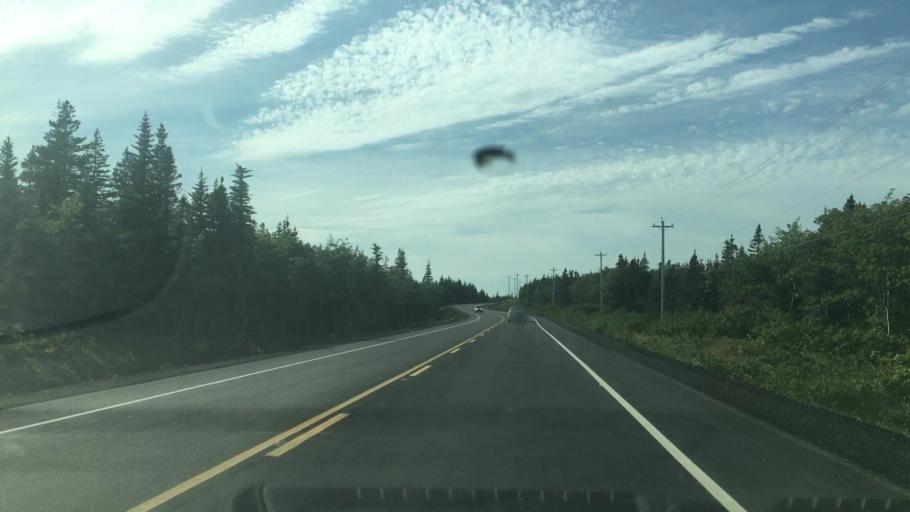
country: CA
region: Nova Scotia
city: Sydney Mines
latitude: 46.8424
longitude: -60.3972
